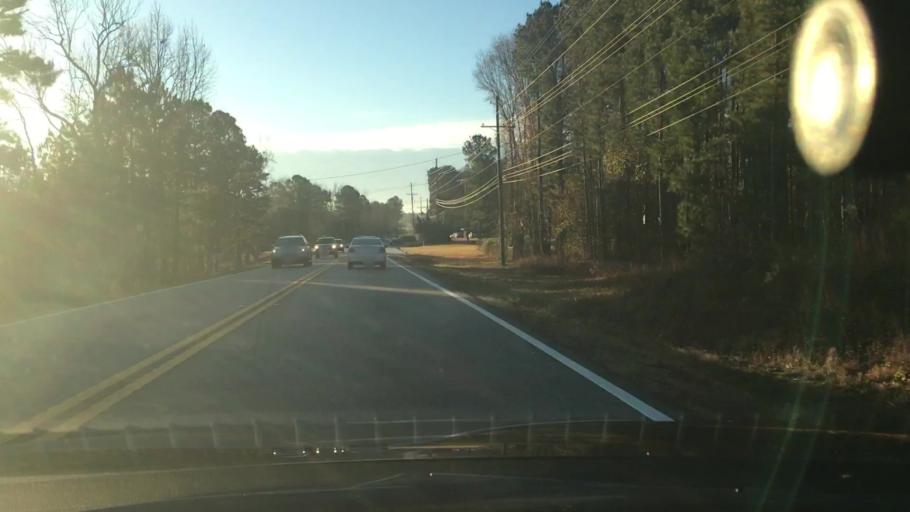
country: US
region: Georgia
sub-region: Fayette County
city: Peachtree City
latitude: 33.3940
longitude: -84.6779
